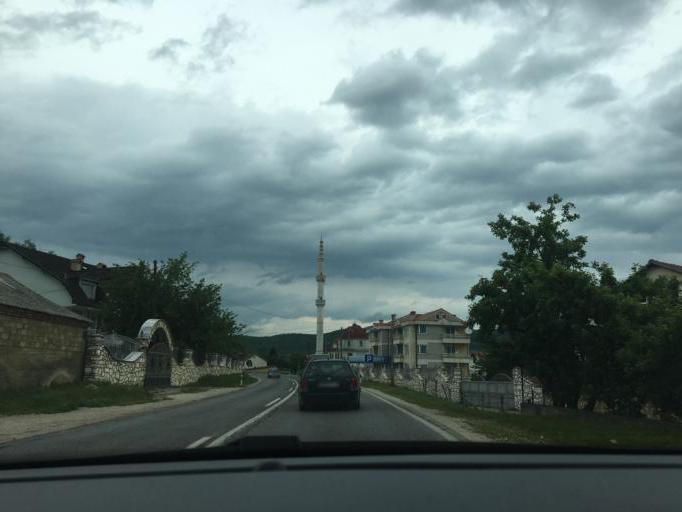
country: MK
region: Kicevo
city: Kicevo
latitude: 41.5572
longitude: 20.9634
